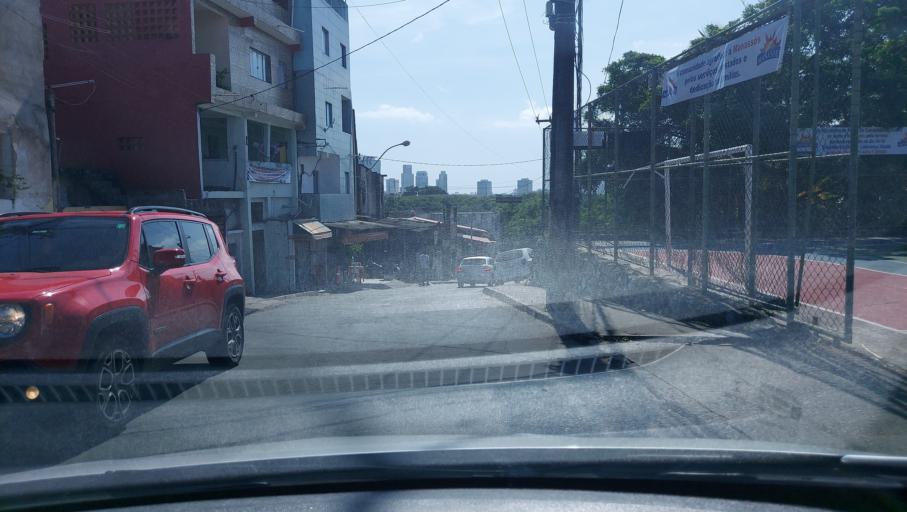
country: BR
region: Bahia
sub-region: Salvador
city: Salvador
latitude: -12.9769
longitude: -38.4403
